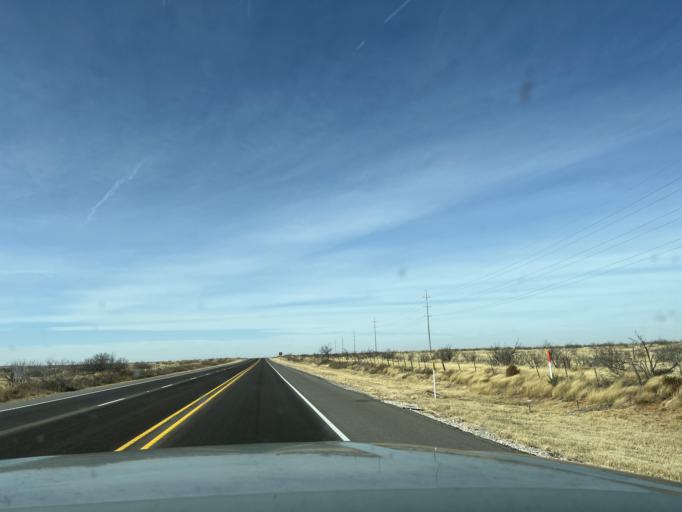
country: US
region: Texas
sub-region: Andrews County
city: Andrews
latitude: 32.3543
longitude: -102.7545
